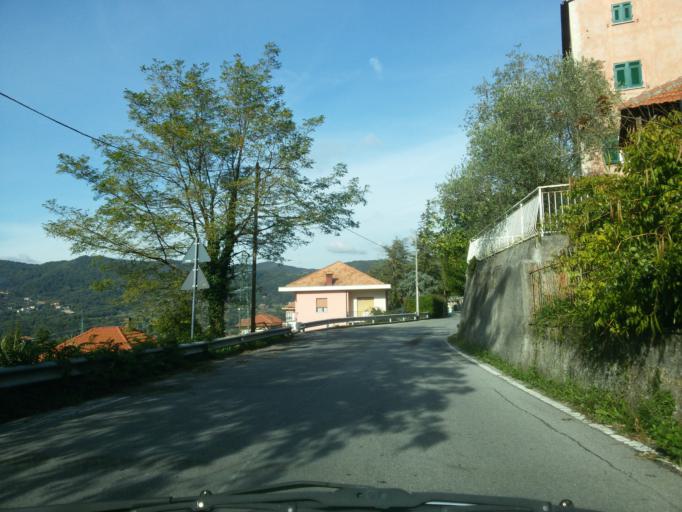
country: IT
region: Liguria
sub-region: Provincia di Genova
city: Piccarello
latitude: 44.4720
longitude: 8.9595
